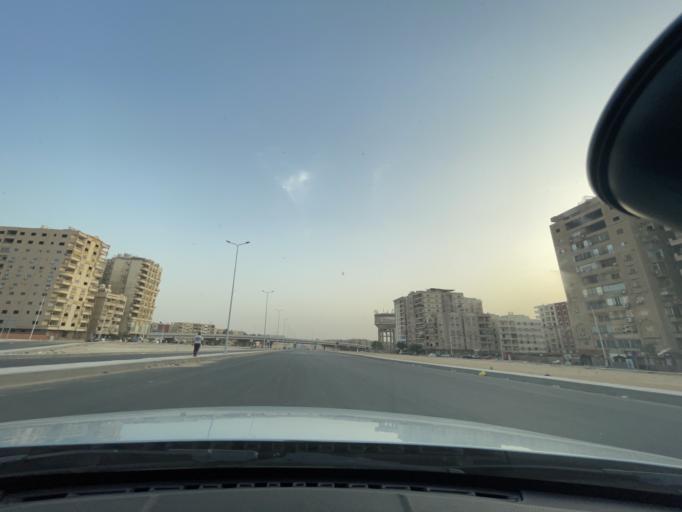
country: EG
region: Muhafazat al Qahirah
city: Cairo
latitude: 30.0499
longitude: 31.3679
